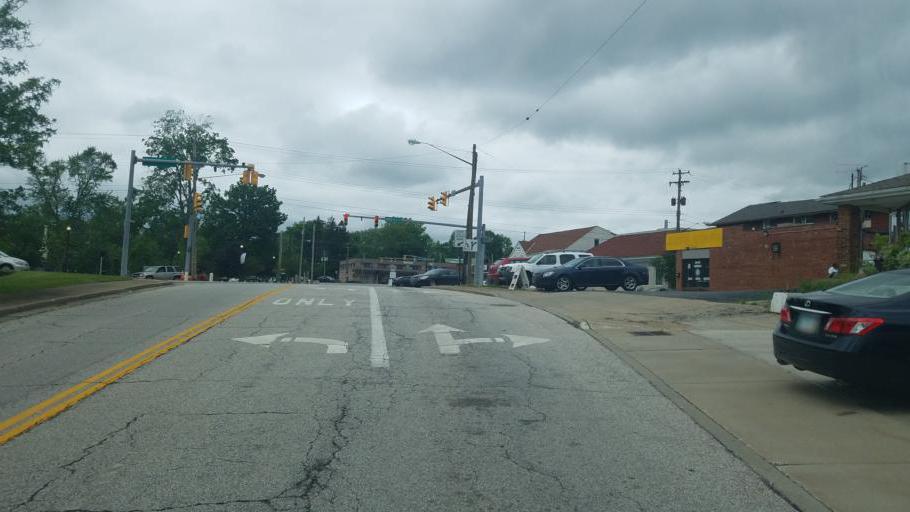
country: US
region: Ohio
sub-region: Summit County
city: Twinsburg
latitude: 41.3125
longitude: -81.4396
